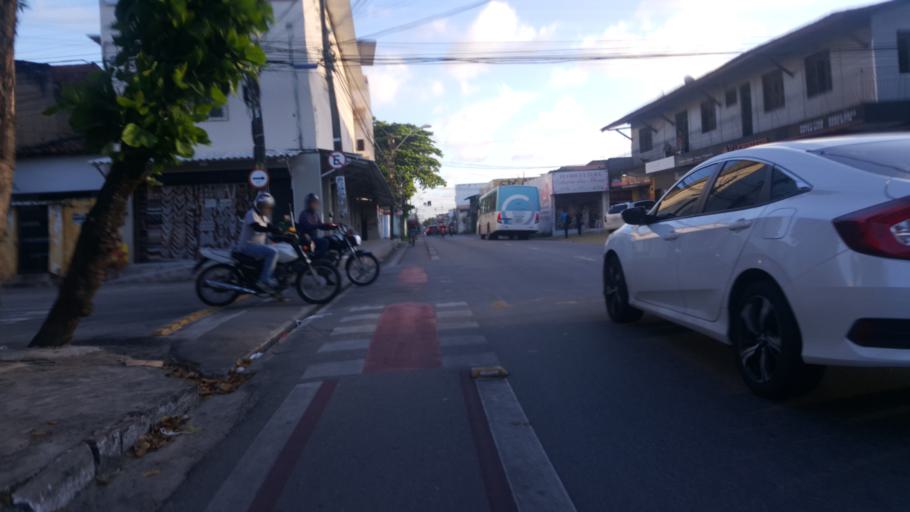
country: BR
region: Ceara
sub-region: Fortaleza
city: Fortaleza
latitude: -3.7566
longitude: -38.5427
